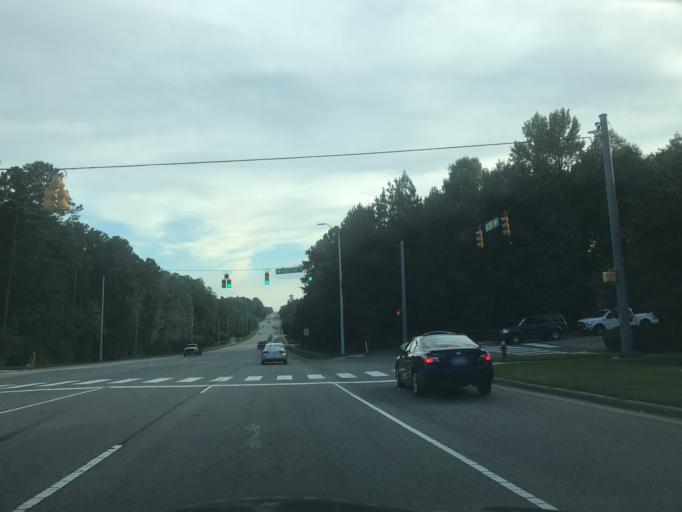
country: US
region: North Carolina
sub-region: Wake County
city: Green Level
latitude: 35.7847
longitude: -78.8713
